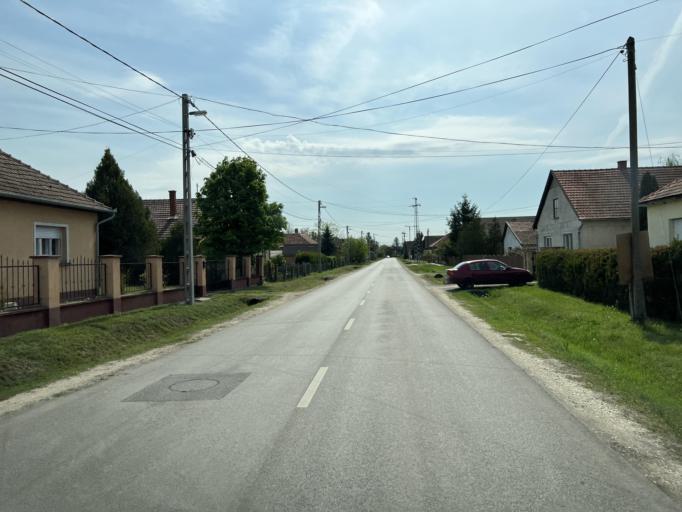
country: HU
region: Pest
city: Tapioszolos
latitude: 47.2869
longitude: 19.8505
